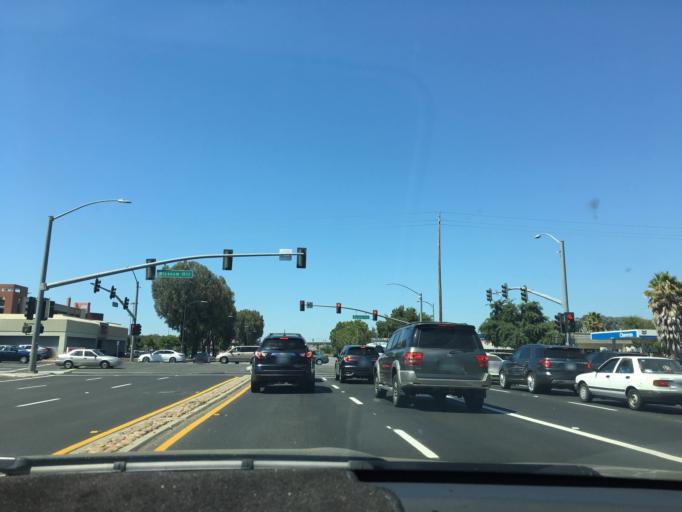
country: US
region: California
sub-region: Santa Clara County
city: Seven Trees
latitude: 37.2498
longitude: -121.8589
